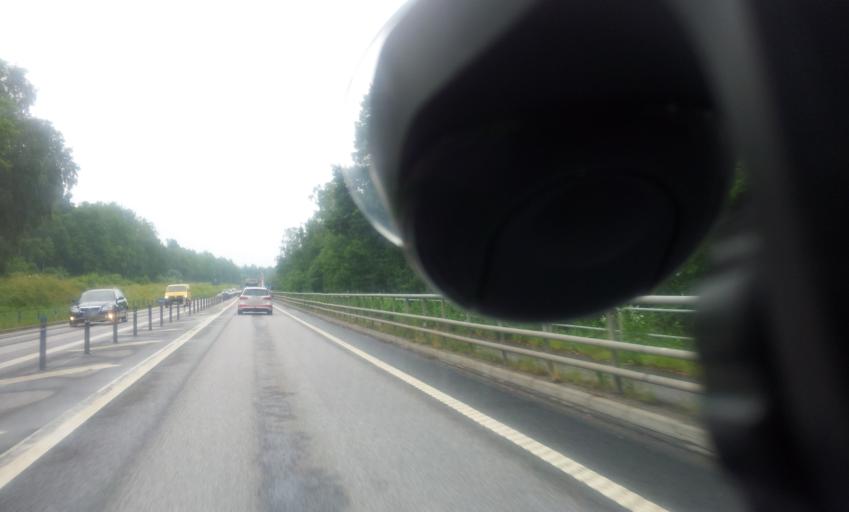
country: SE
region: Kalmar
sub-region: Vasterviks Kommun
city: Vaestervik
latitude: 57.8001
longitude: 16.5128
